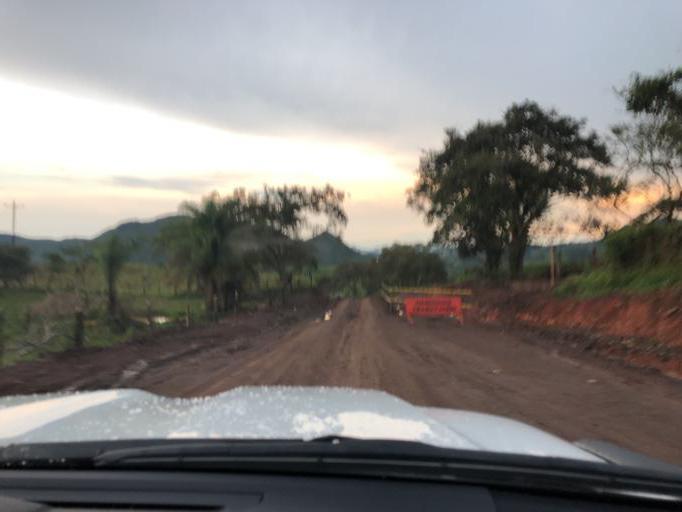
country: NI
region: Chontales
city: La Libertad
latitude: 12.1886
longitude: -85.1746
